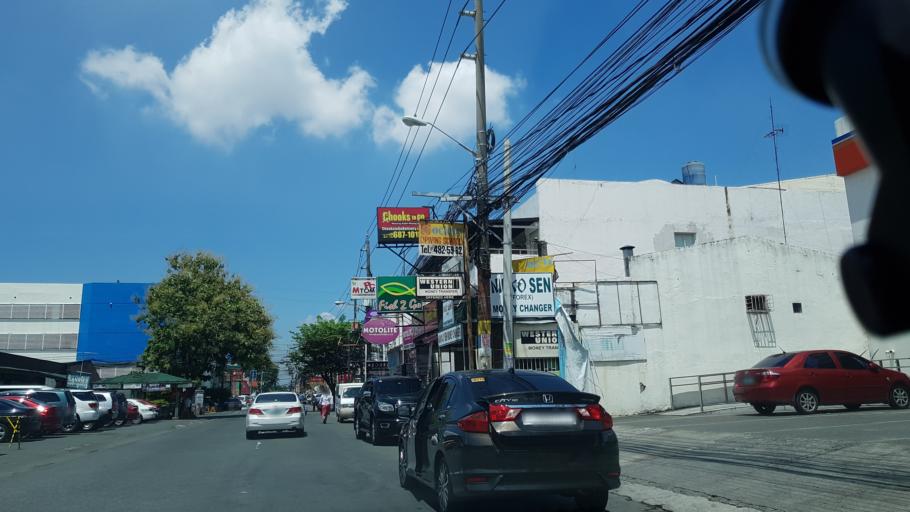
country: PH
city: Sambayanihan People's Village
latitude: 14.4454
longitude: 121.0288
